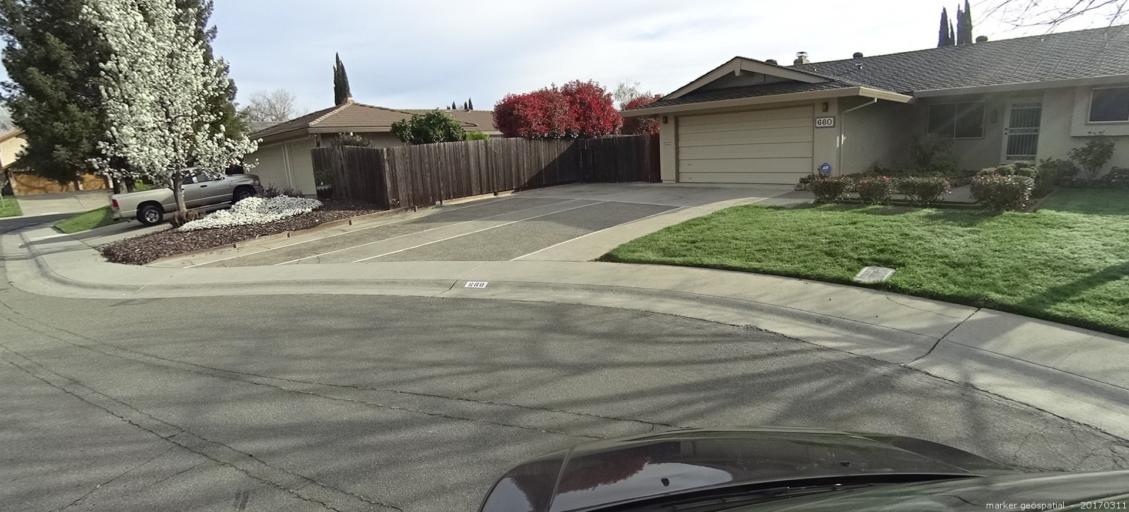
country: US
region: California
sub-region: Yolo County
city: West Sacramento
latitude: 38.5150
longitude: -121.5383
